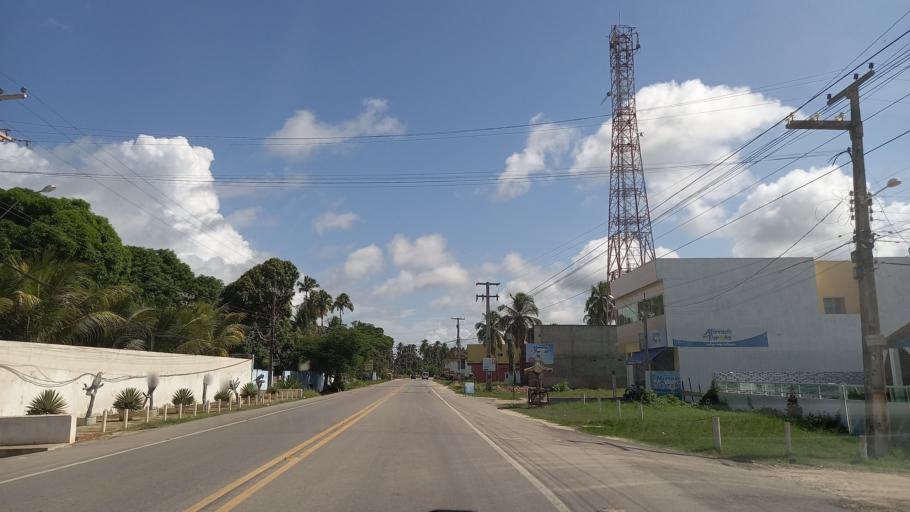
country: BR
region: Pernambuco
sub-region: Sao Jose Da Coroa Grande
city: Sao Jose da Coroa Grande
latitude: -8.9249
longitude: -35.1605
